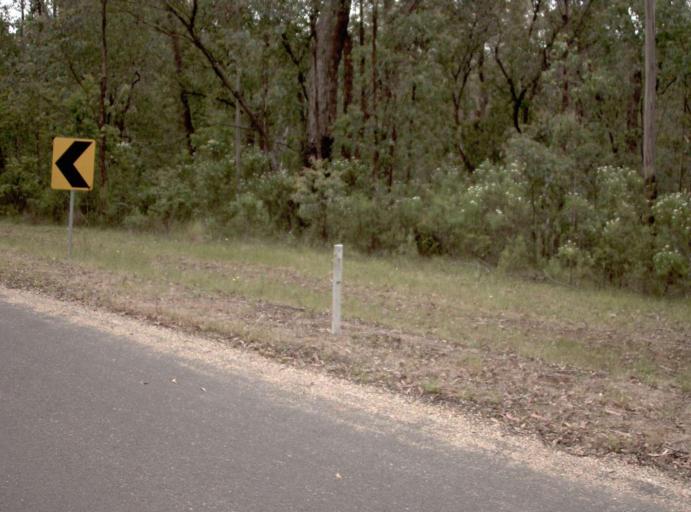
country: AU
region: Victoria
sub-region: East Gippsland
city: Bairnsdale
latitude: -37.6381
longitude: 147.2475
